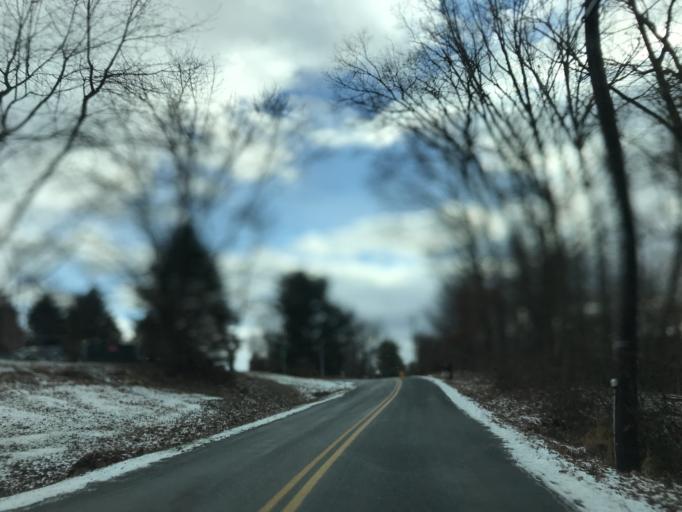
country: US
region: Maryland
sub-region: Harford County
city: Jarrettsville
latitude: 39.6264
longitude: -76.4792
